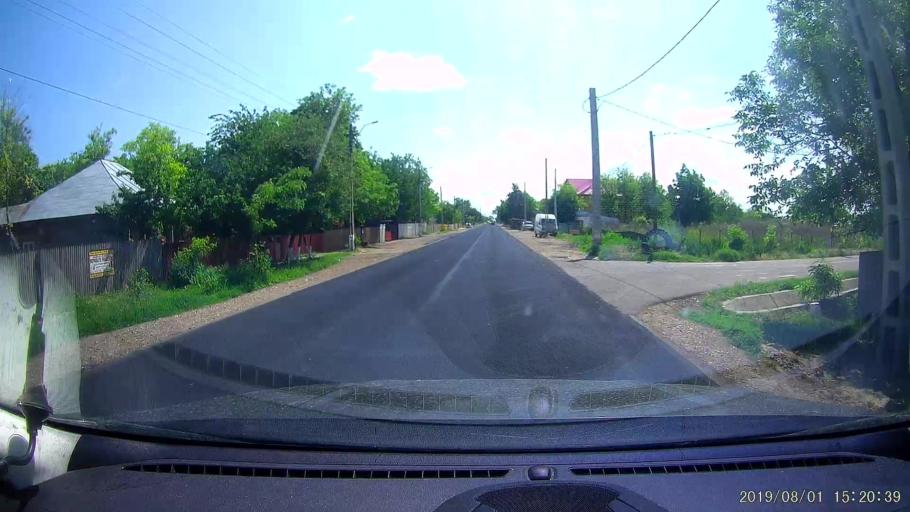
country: RO
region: Braila
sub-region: Comuna Tufesti
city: Tufesti
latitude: 45.0772
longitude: 27.8048
